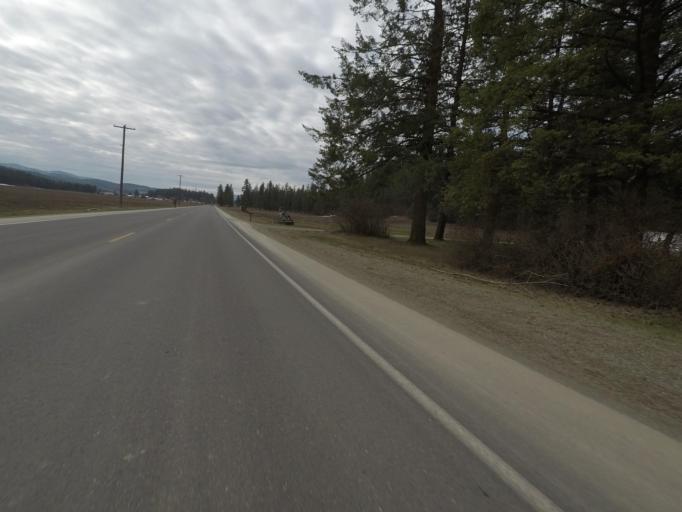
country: US
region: Washington
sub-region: Stevens County
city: Colville
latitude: 48.5689
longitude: -117.8793
